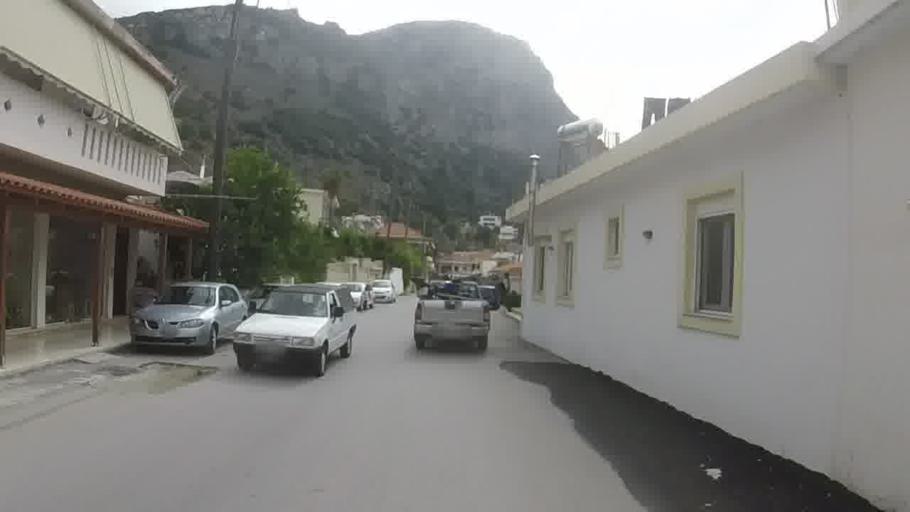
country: GR
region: Crete
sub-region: Nomos Rethymnis
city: Agia Foteini
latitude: 35.2189
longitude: 24.5343
